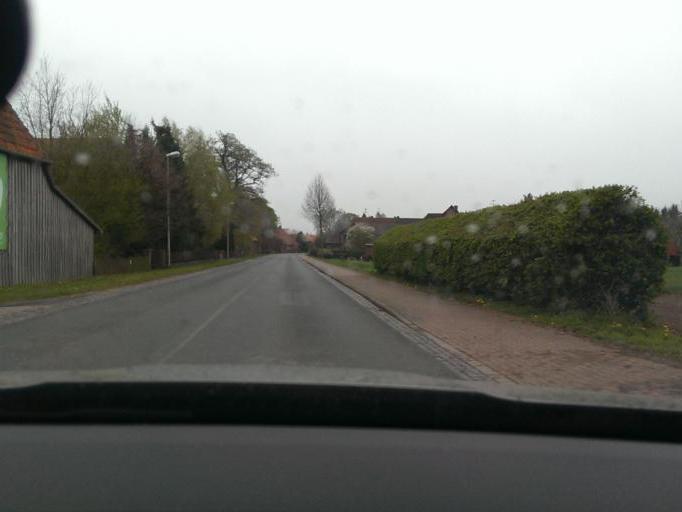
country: DE
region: Lower Saxony
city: Steimbke
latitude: 52.6515
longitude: 9.4882
